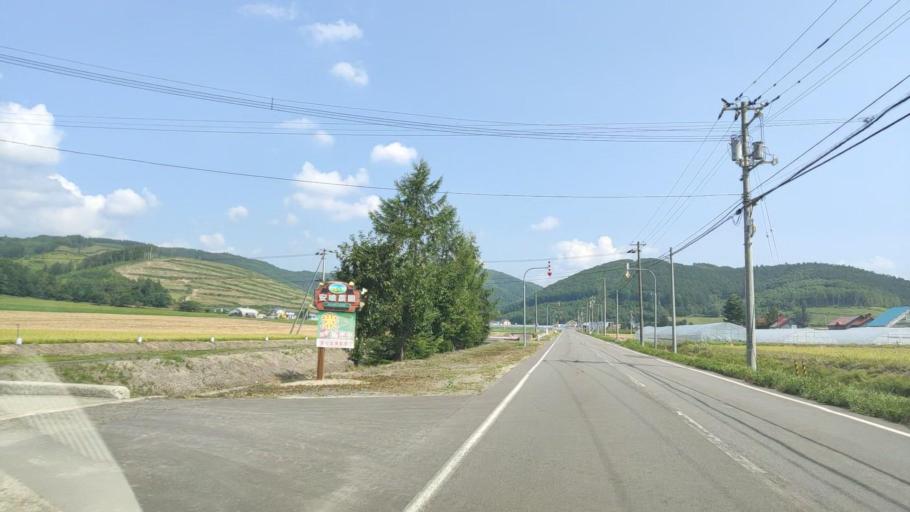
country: JP
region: Hokkaido
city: Shimo-furano
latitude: 43.4125
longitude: 142.3985
